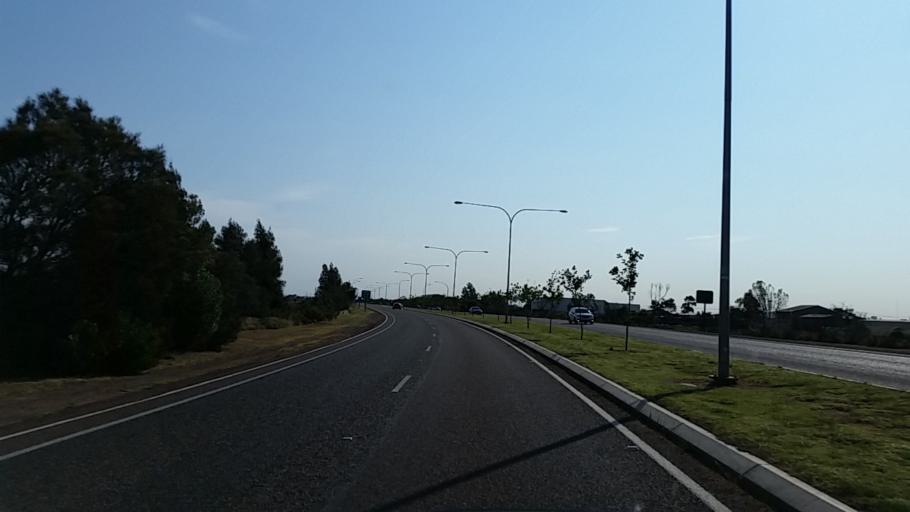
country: AU
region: South Australia
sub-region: Whyalla
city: Whyalla
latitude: -33.0399
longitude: 137.5558
